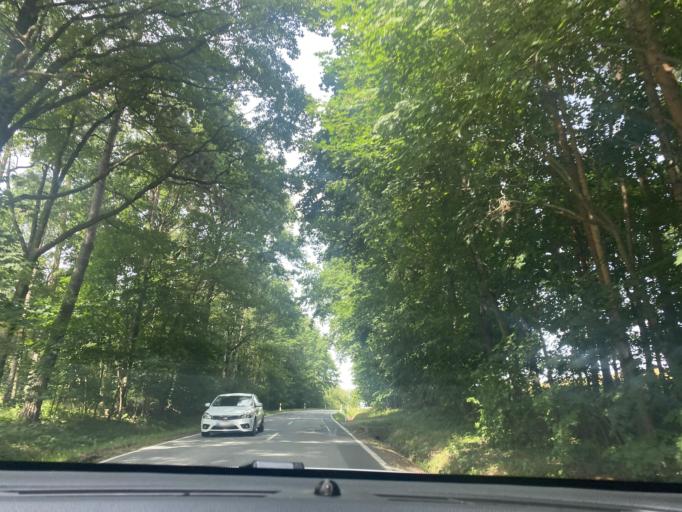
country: DE
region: Saxony
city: Grosshennersdorf
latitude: 51.0073
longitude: 14.7951
